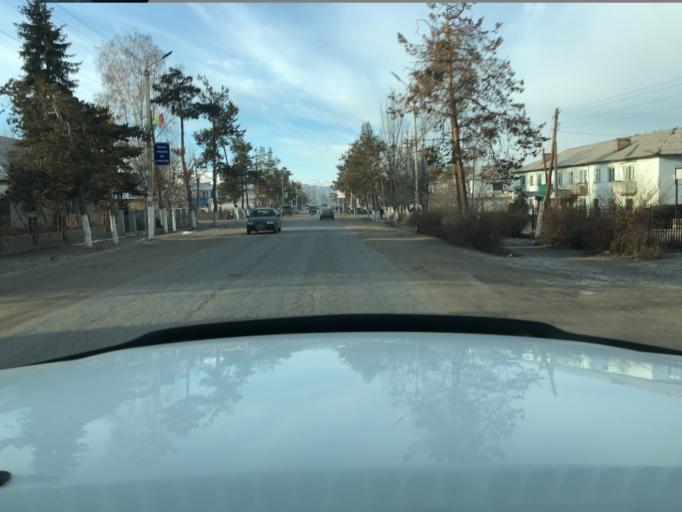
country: KG
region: Ysyk-Koel
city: Pokrovka
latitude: 42.3422
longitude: 78.0049
